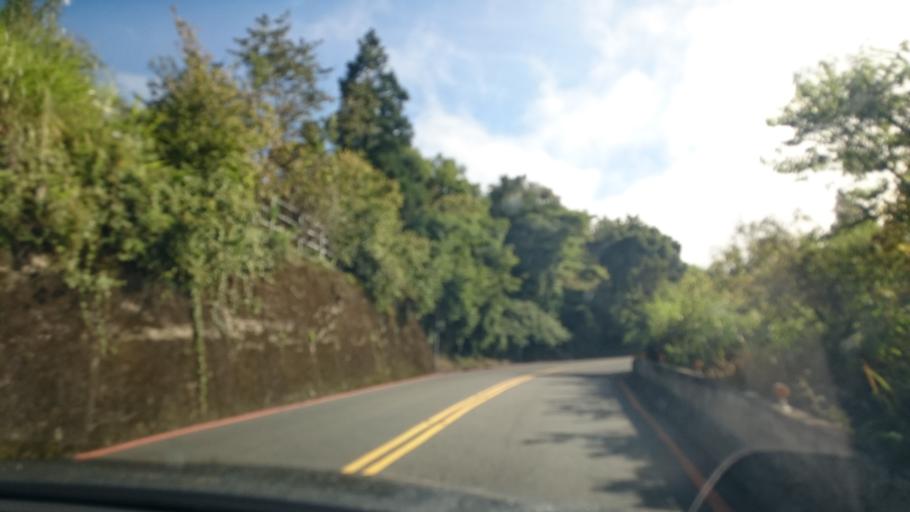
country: TW
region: Taiwan
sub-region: Nantou
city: Puli
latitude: 24.0576
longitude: 121.1633
